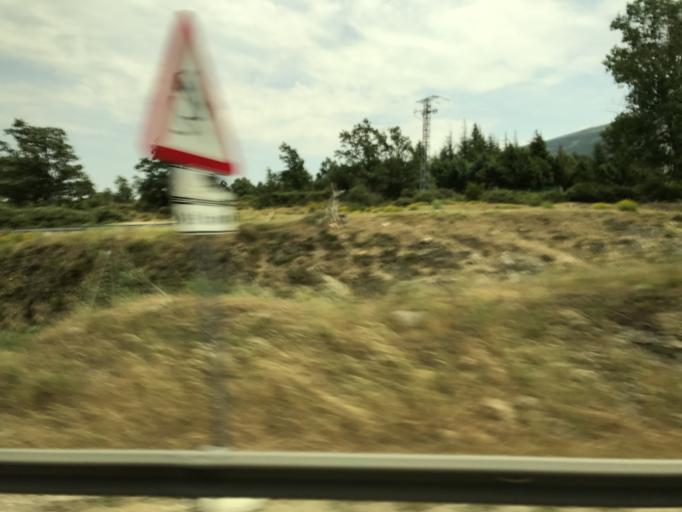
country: ES
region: Madrid
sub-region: Provincia de Madrid
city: Somosierra
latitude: 41.1752
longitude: -3.5798
